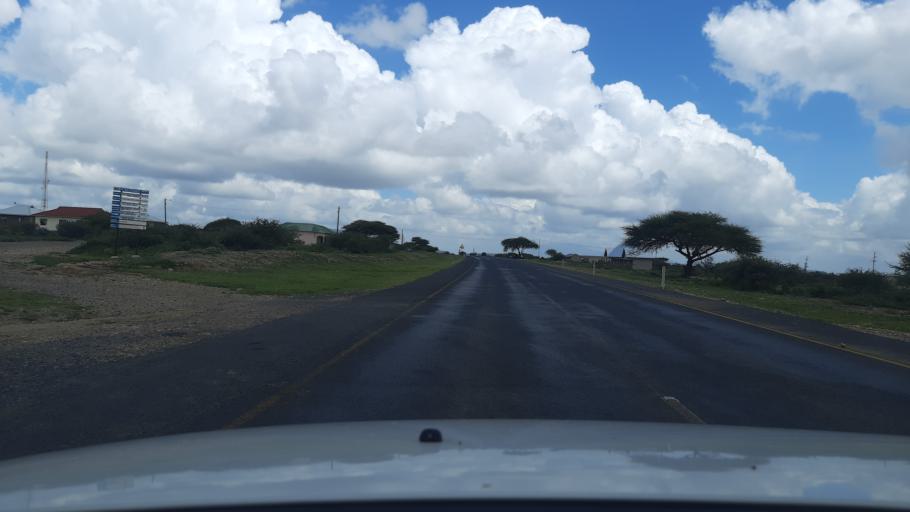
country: TZ
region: Arusha
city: Nkoaranga
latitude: -3.0446
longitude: 36.6979
